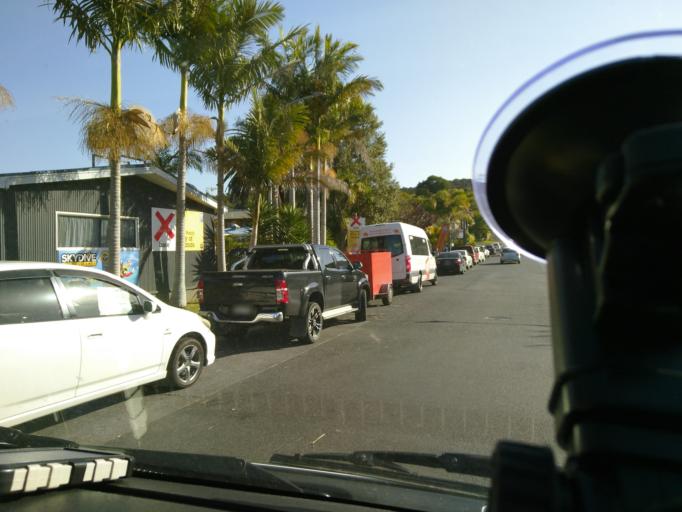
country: NZ
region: Northland
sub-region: Far North District
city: Paihia
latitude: -35.2854
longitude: 174.0950
